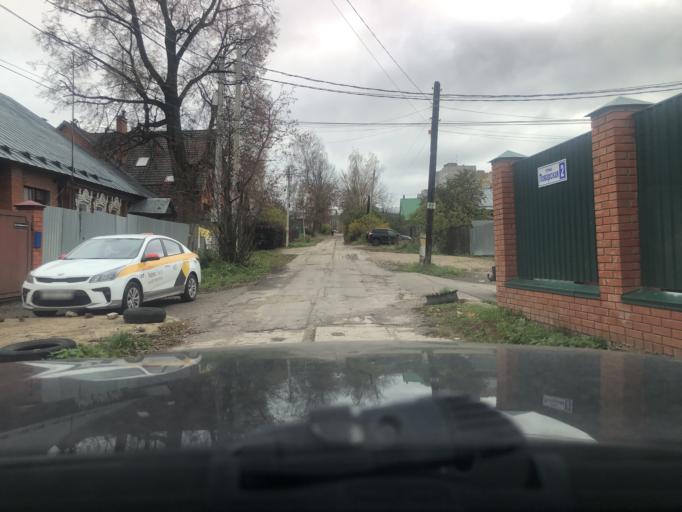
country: RU
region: Moskovskaya
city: Sergiyev Posad
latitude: 56.3014
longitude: 38.1191
